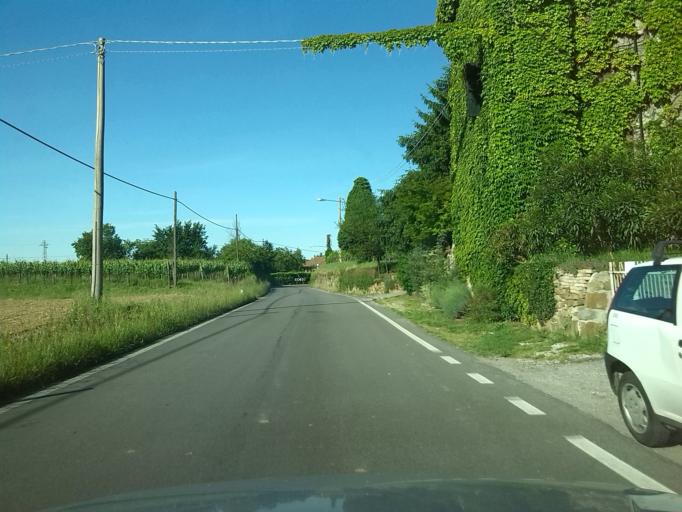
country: IT
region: Friuli Venezia Giulia
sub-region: Provincia di Gorizia
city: Cormons
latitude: 45.9576
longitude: 13.4847
